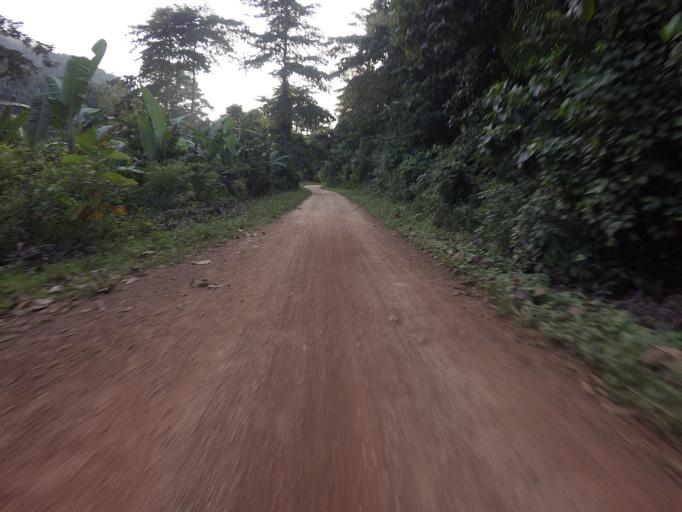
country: GH
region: Volta
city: Kpandu
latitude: 6.8779
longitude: 0.4433
